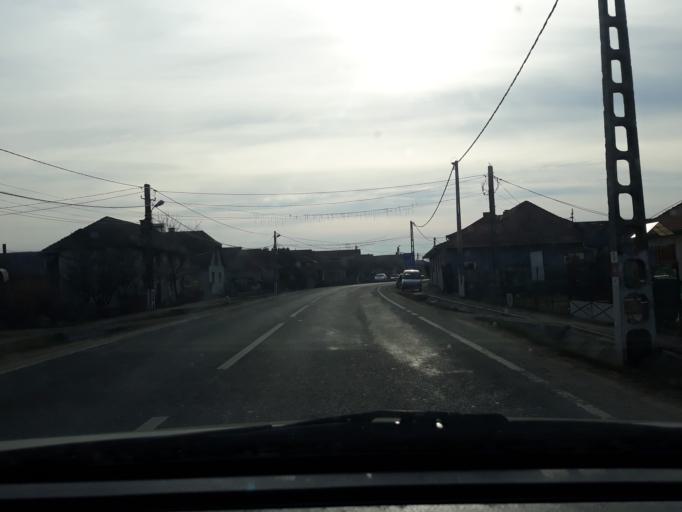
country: RO
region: Salaj
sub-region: Comuna Varsolt
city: Varsolt
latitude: 47.2105
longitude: 22.9207
